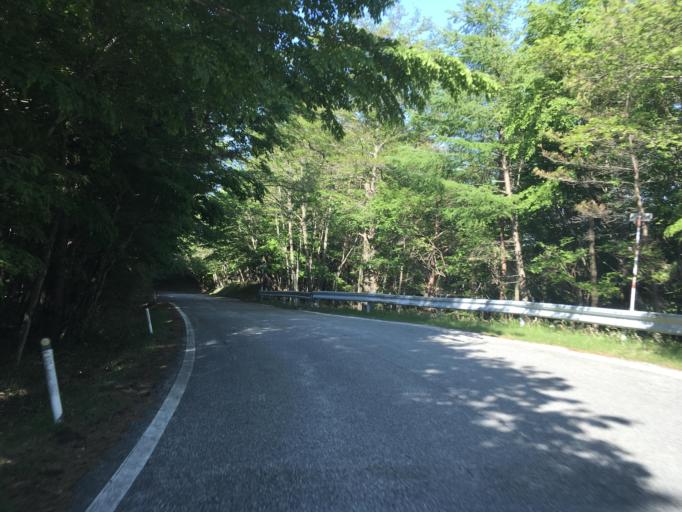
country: JP
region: Iwate
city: Ofunato
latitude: 39.1831
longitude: 141.7530
